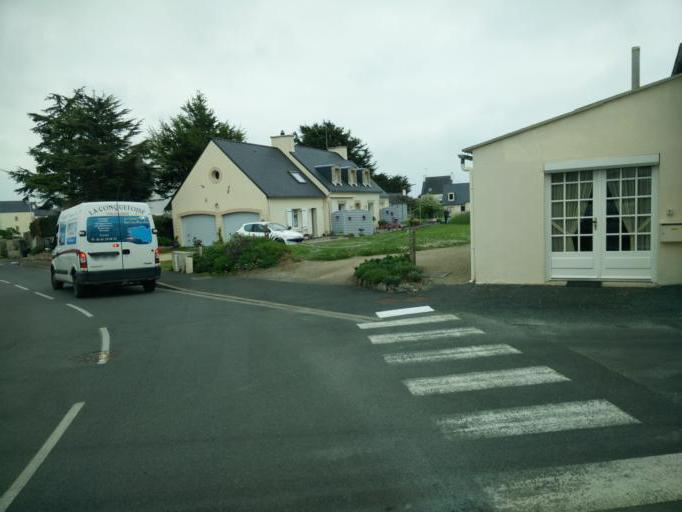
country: FR
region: Brittany
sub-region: Departement du Finistere
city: Plobannalec-Lesconil
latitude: 47.8005
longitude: -4.2190
